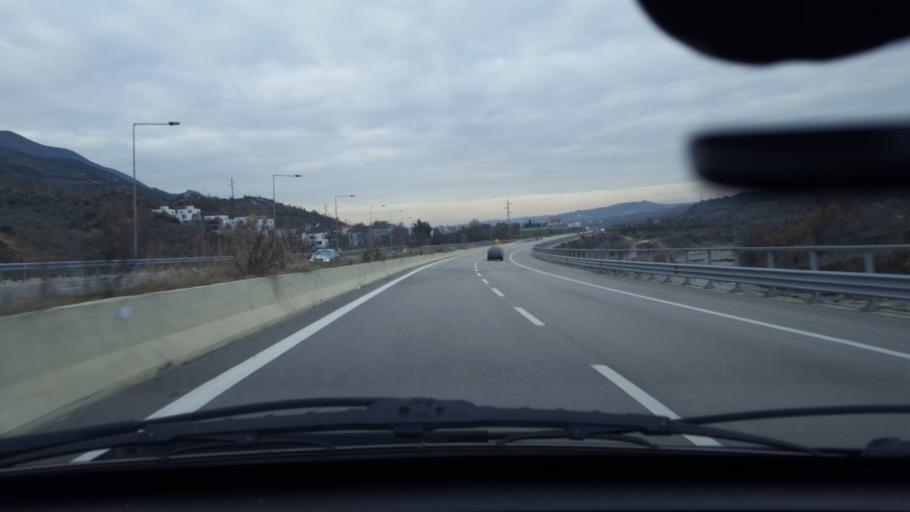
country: AL
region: Tirane
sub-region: Rrethi i Tiranes
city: Berzhite
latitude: 41.2357
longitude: 19.9186
